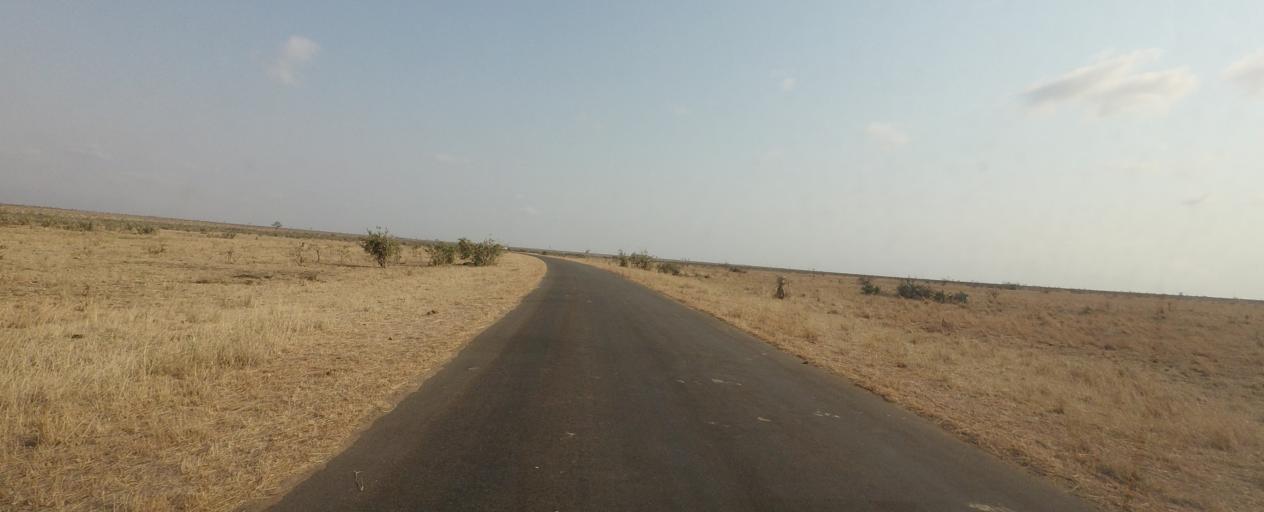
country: ZA
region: Limpopo
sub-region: Vhembe District Municipality
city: Mutale
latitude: -22.9467
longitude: 31.2872
